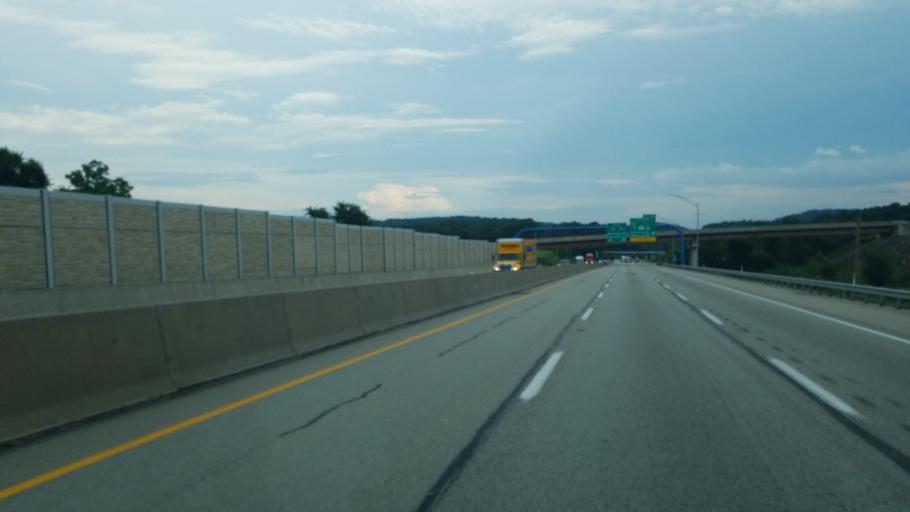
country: US
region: Pennsylvania
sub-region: Westmoreland County
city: New Stanton
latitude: 40.2273
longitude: -79.6113
